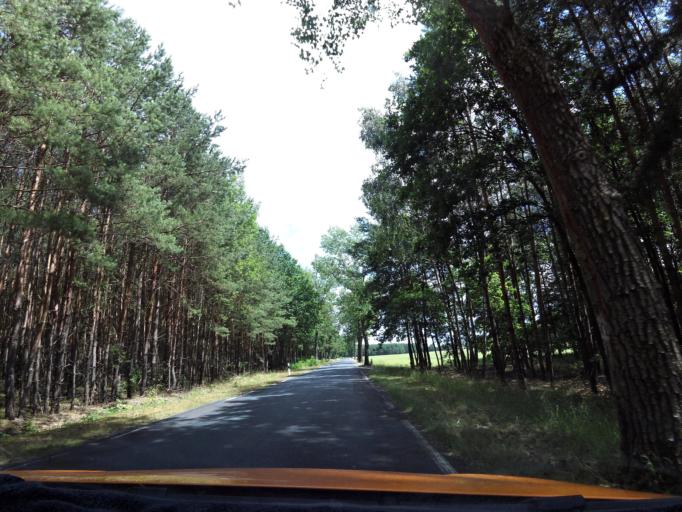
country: DE
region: Brandenburg
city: Storkow
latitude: 52.2458
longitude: 13.8532
